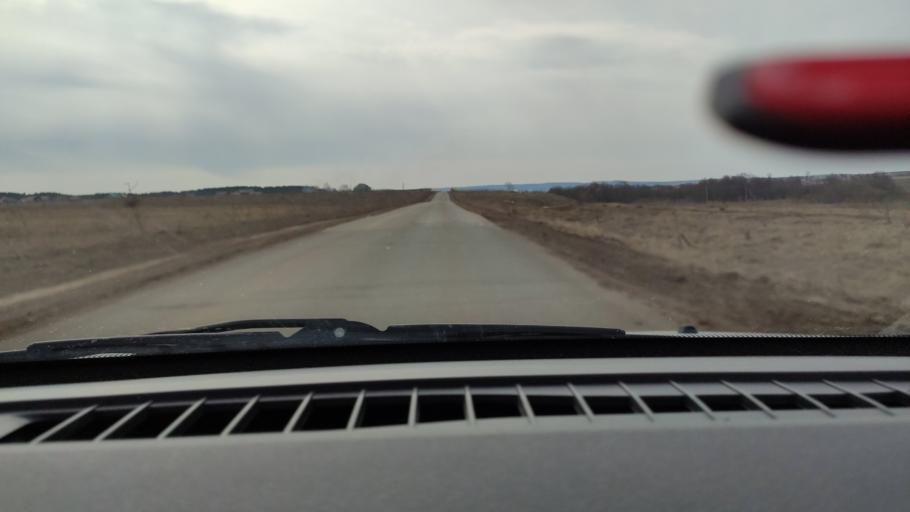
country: RU
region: Perm
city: Kultayevo
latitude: 57.9039
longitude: 55.9920
